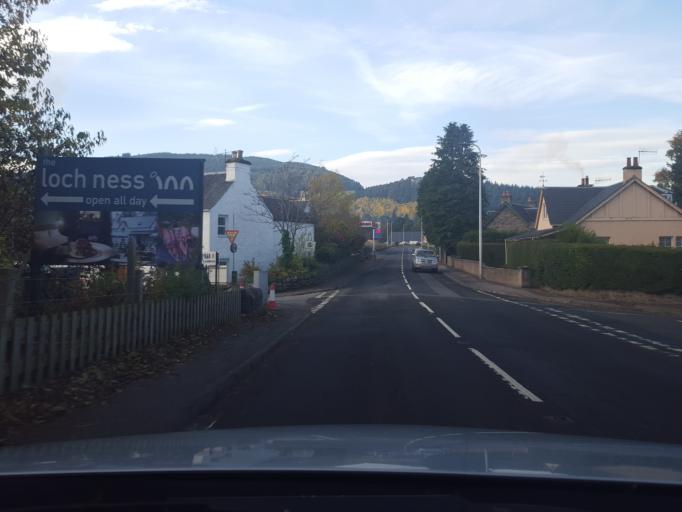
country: GB
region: Scotland
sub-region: Highland
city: Beauly
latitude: 57.3281
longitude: -4.4728
